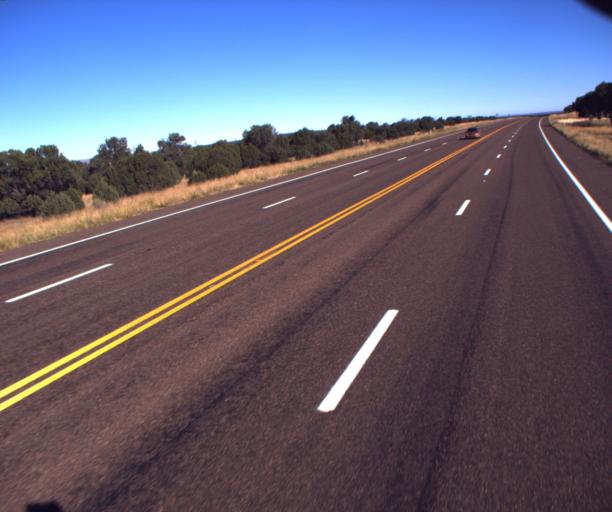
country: US
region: Arizona
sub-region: Navajo County
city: White Mountain Lake
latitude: 34.3489
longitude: -110.0530
